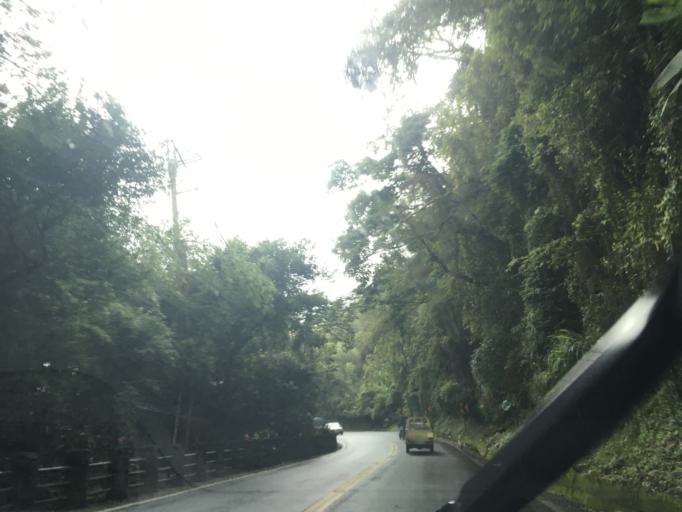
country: TW
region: Taiwan
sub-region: Chiayi
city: Jiayi Shi
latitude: 23.4483
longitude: 120.6772
